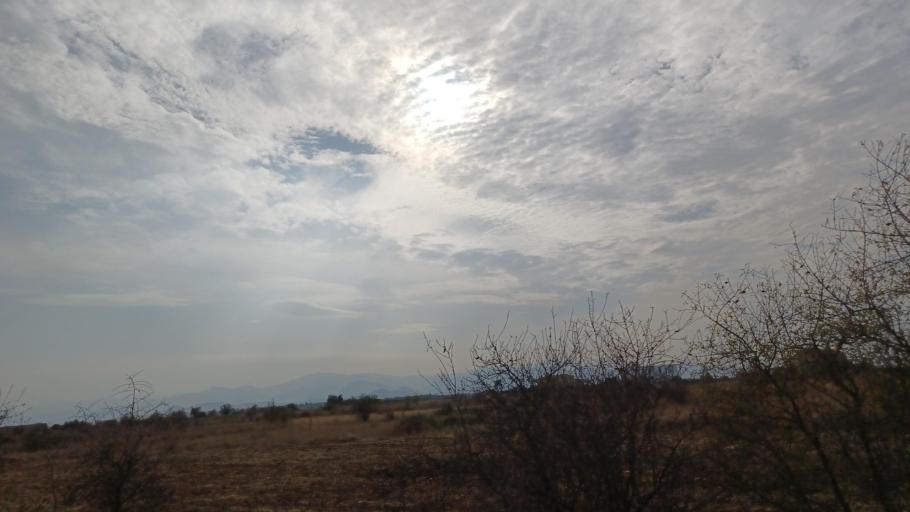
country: CY
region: Lefkosia
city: Peristerona
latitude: 35.1232
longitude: 33.0917
